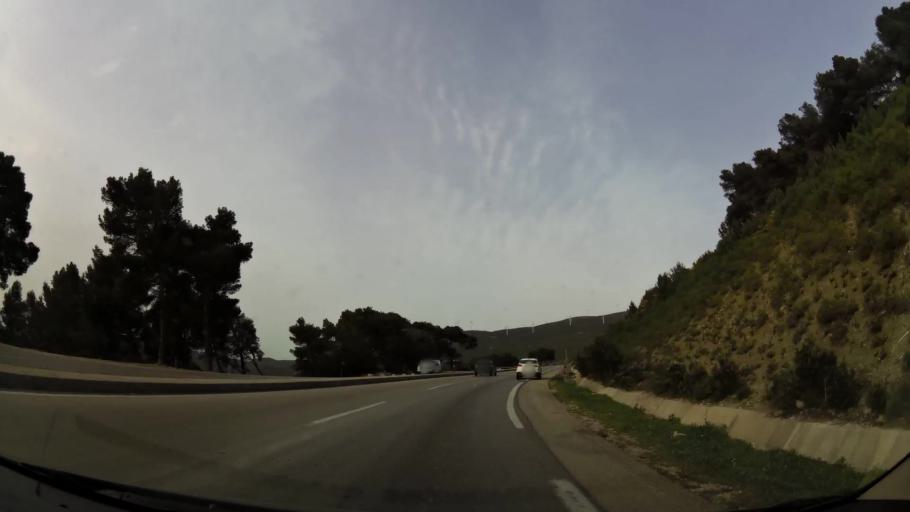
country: MA
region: Tanger-Tetouan
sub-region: Tanger-Assilah
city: Dar Chaoui
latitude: 35.5601
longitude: -5.5822
